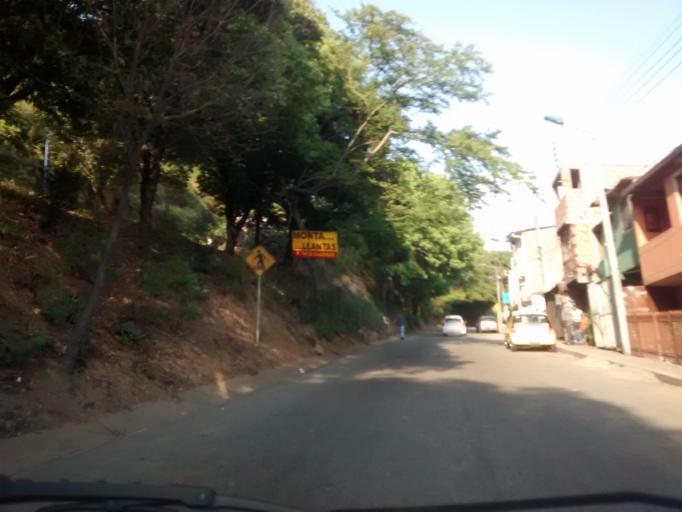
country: CO
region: Santander
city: Bucaramanga
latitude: 7.0944
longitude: -73.1285
